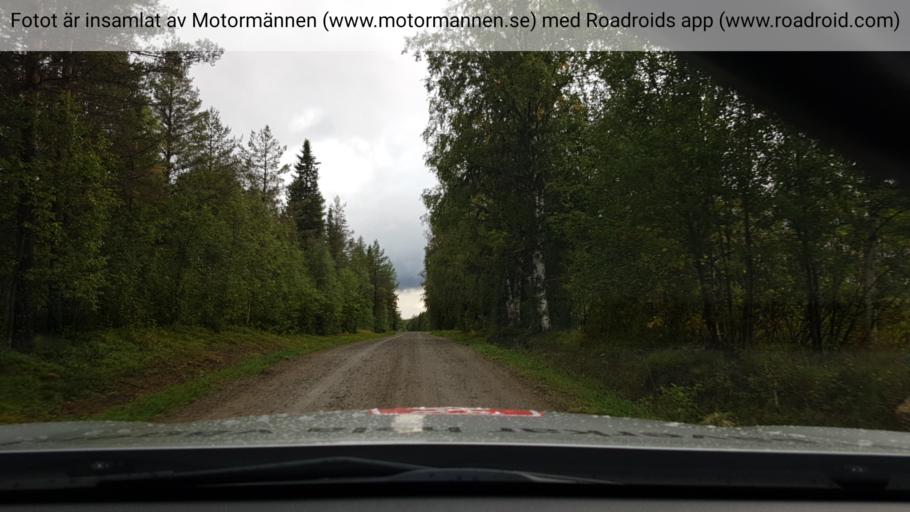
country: SE
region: Vaesterbotten
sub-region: Asele Kommun
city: Asele
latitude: 64.1446
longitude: 16.9022
